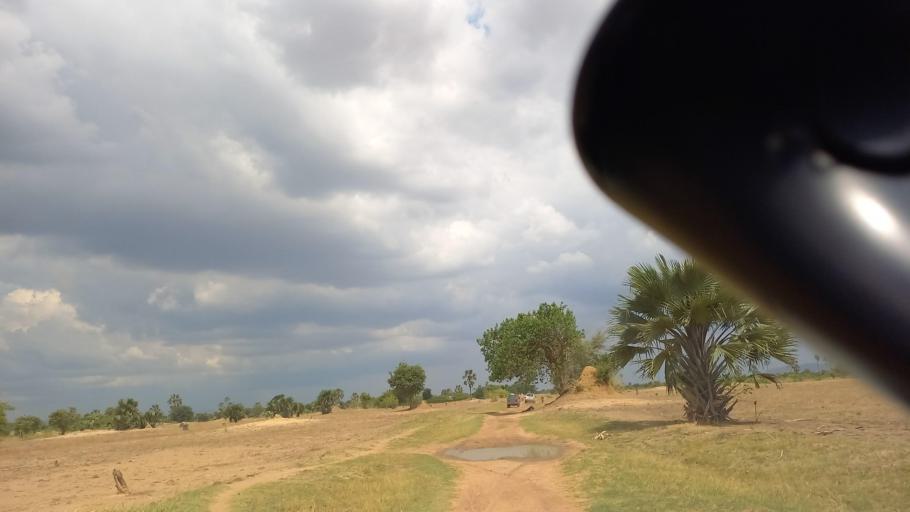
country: ZM
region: Lusaka
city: Kafue
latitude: -15.8307
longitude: 28.0634
